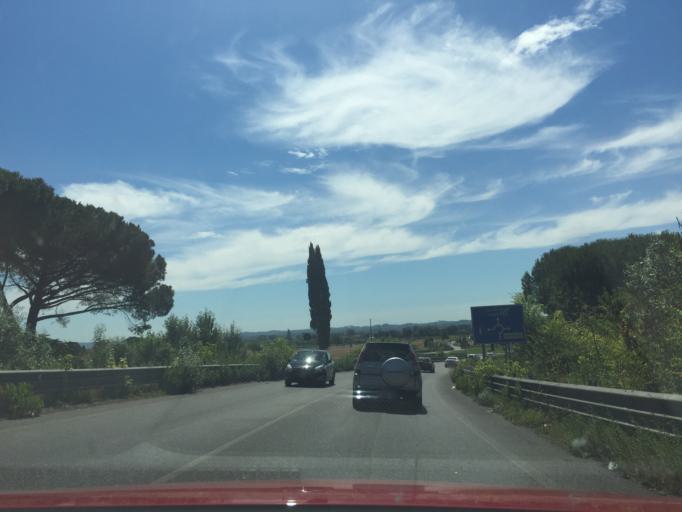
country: IT
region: Tuscany
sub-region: Province of Pisa
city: Pontedera
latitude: 43.6768
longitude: 10.6422
